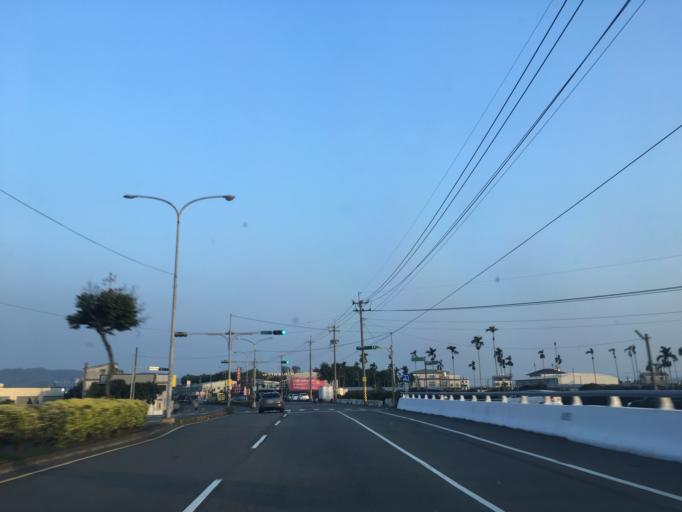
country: TW
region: Taiwan
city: Zhongxing New Village
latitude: 23.9931
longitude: 120.6663
